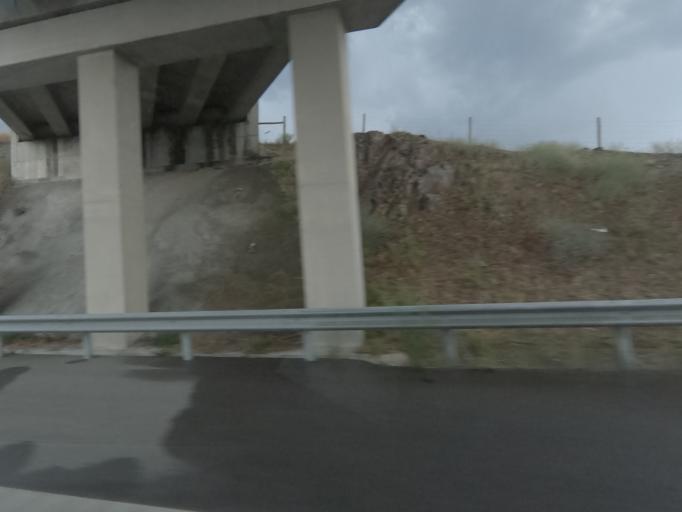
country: PT
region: Vila Real
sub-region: Santa Marta de Penaguiao
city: Santa Marta de Penaguiao
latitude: 41.2245
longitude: -7.7352
